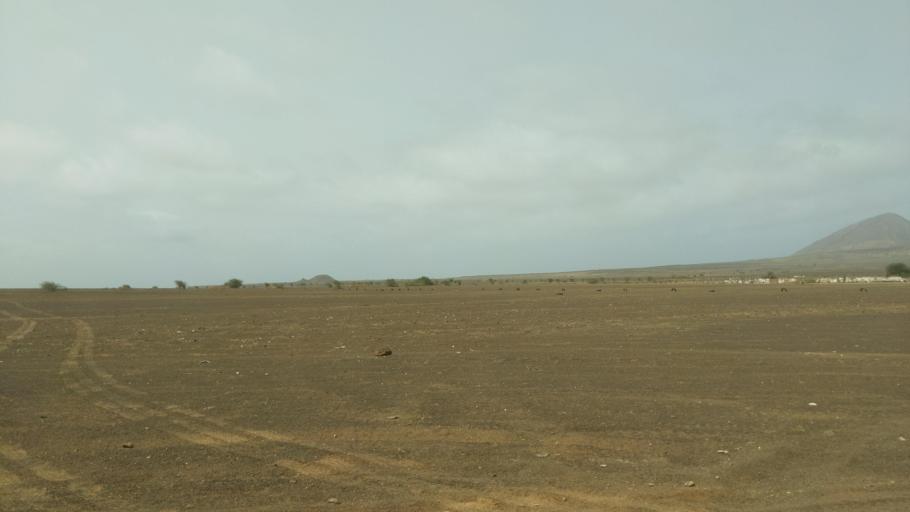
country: CV
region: Sal
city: Espargos
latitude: 16.7971
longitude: -22.9557
